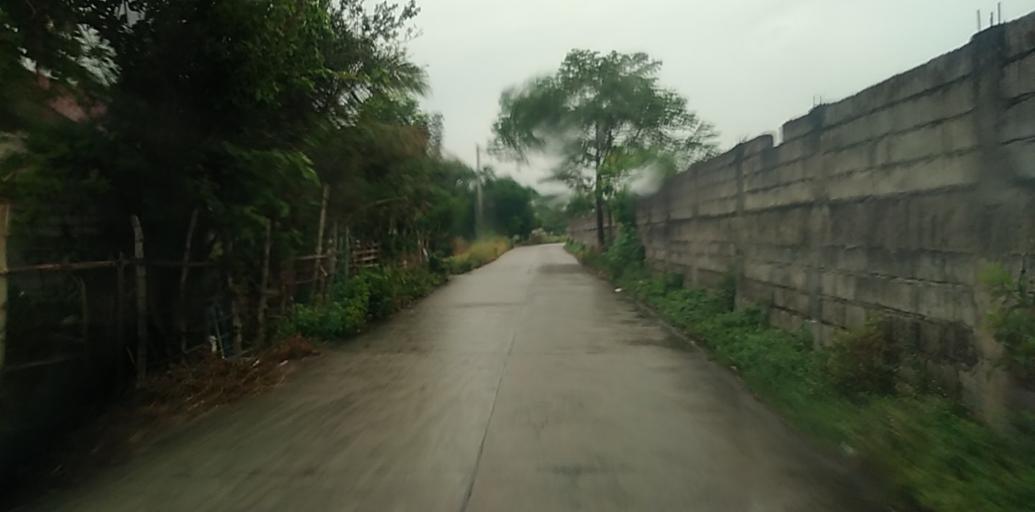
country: PH
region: Central Luzon
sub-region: Province of Pampanga
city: Anao
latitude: 15.1383
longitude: 120.6964
